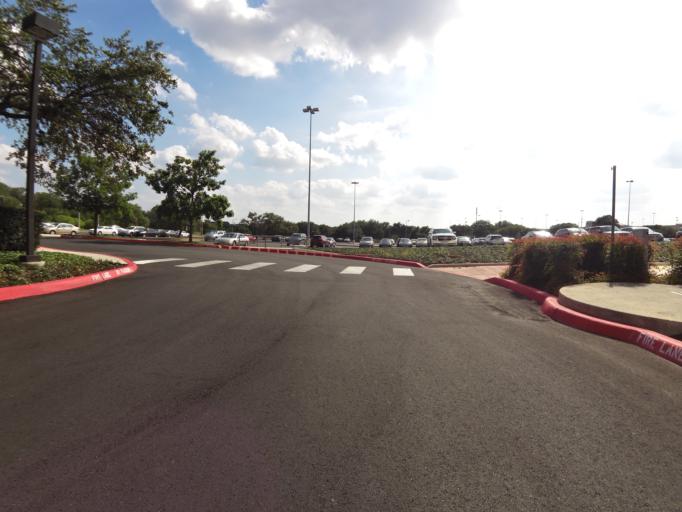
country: US
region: Texas
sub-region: Bexar County
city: Shavano Park
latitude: 29.5808
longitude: -98.6176
